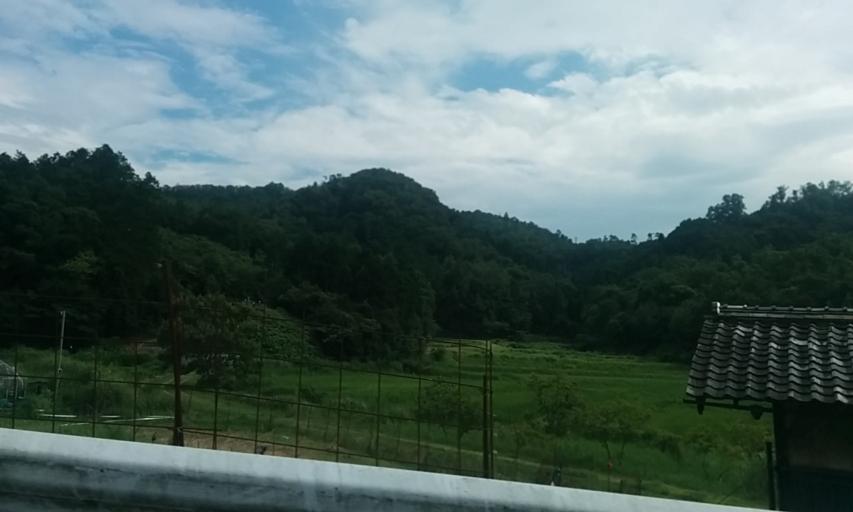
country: JP
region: Kyoto
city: Maizuru
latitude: 35.3561
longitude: 135.3339
